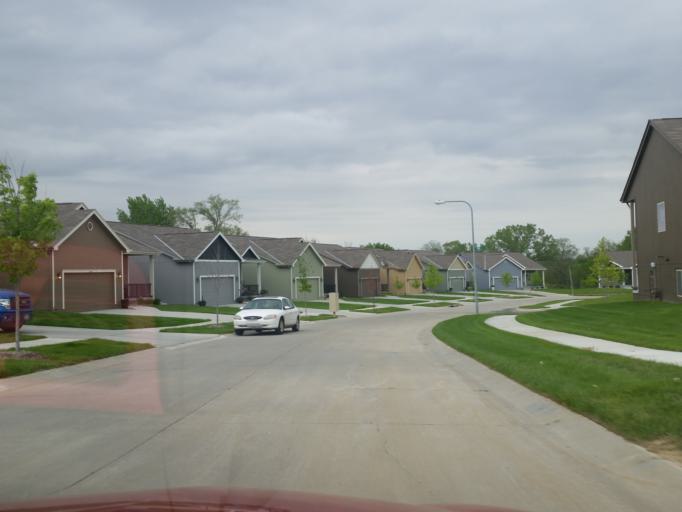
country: US
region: Nebraska
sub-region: Douglas County
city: Bennington
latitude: 41.3221
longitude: -96.1305
